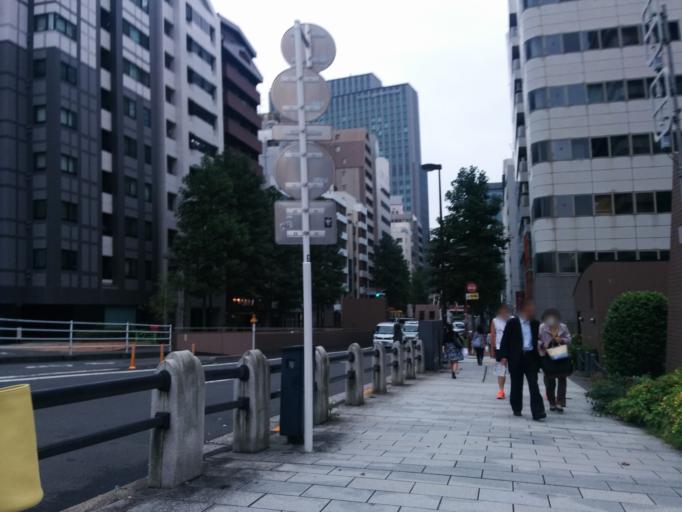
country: JP
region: Tokyo
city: Tokyo
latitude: 35.6657
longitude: 139.7661
